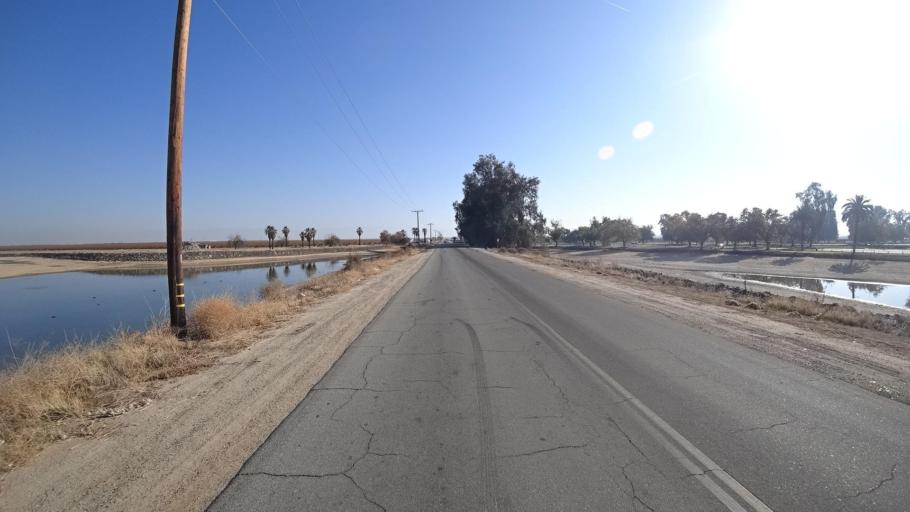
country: US
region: California
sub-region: Kern County
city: Delano
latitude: 35.7470
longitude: -119.1778
